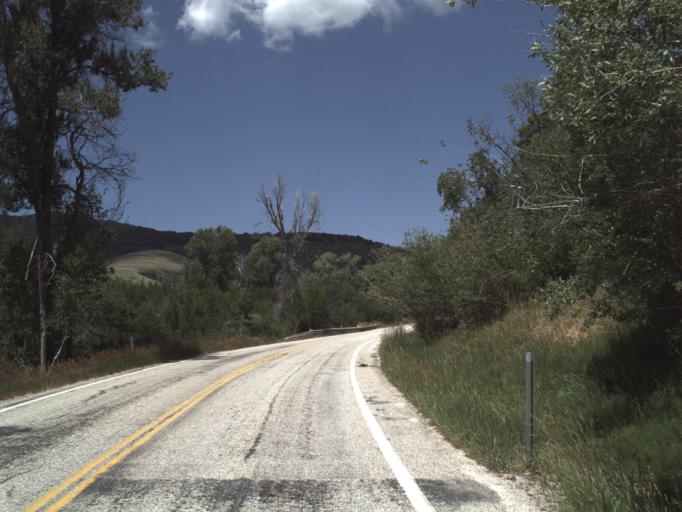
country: US
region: Utah
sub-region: Weber County
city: Wolf Creek
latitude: 41.3145
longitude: -111.6152
